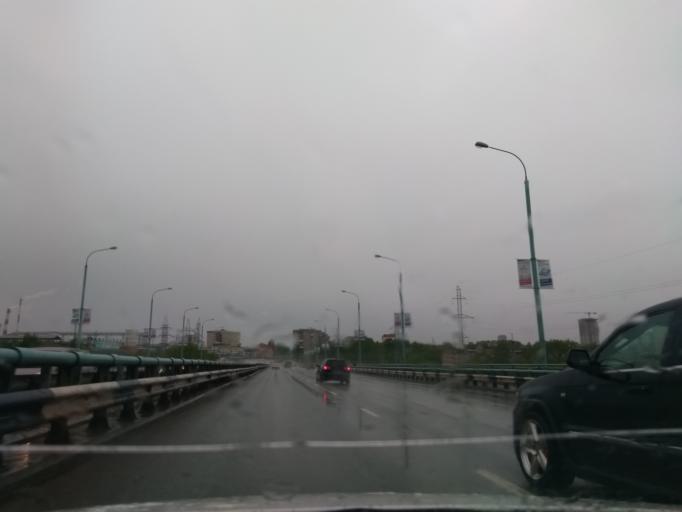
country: RU
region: Perm
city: Perm
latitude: 57.9861
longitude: 56.2823
